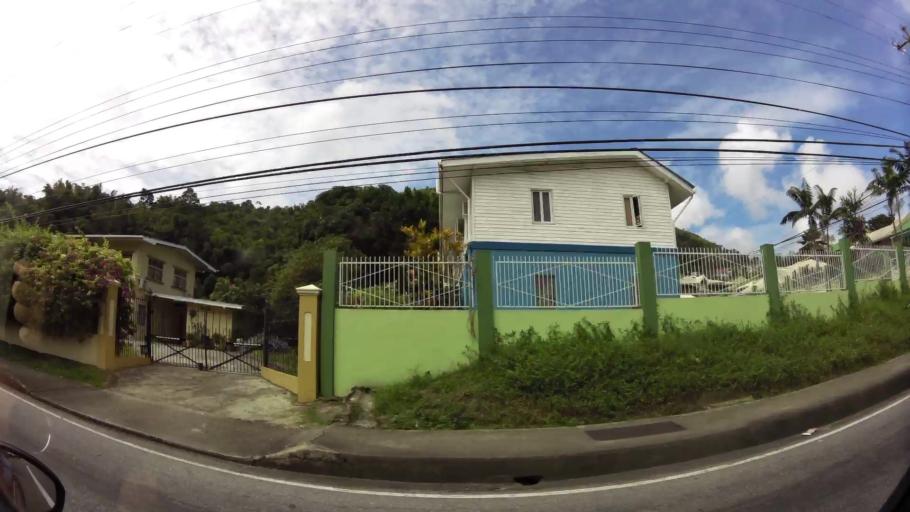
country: TT
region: Diego Martin
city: Petit Valley
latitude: 10.6991
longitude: -61.5562
